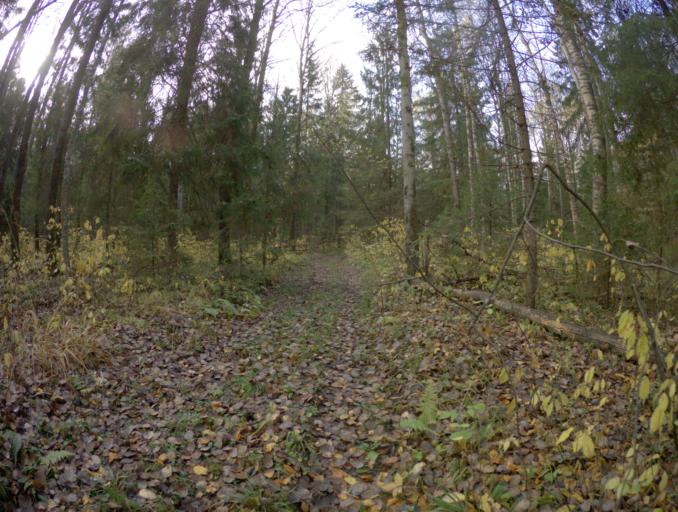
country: RU
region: Vladimir
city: Raduzhnyy
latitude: 55.9660
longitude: 40.3723
